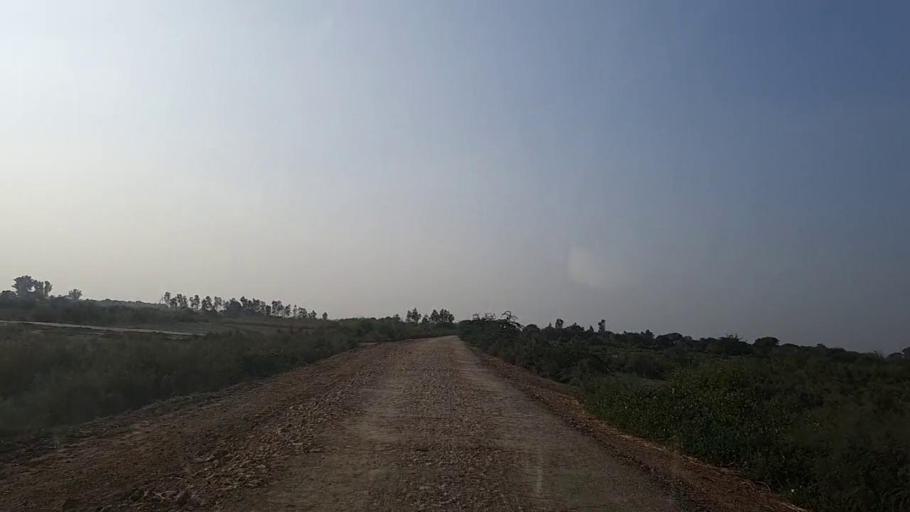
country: PK
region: Sindh
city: Mirpur Sakro
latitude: 24.5696
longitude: 67.6696
